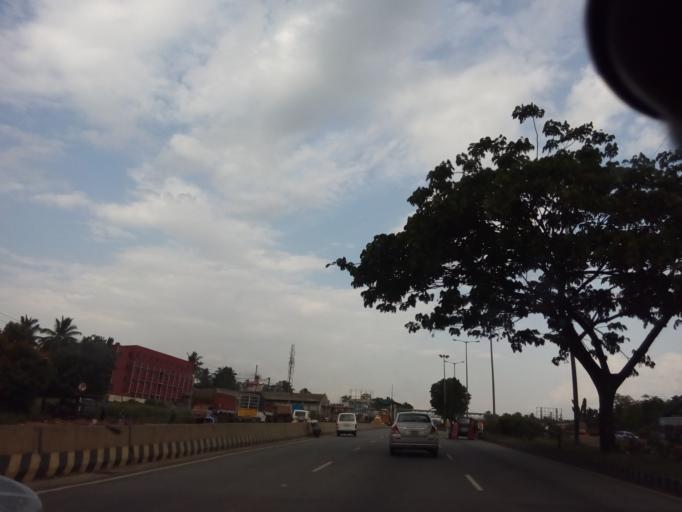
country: IN
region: Karnataka
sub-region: Bangalore Rural
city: Nelamangala
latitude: 13.0558
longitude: 77.4774
